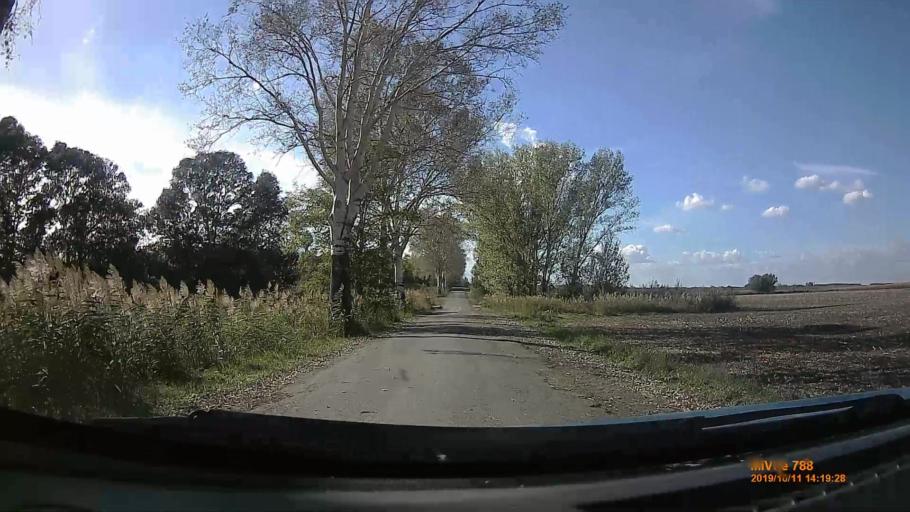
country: HU
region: Hajdu-Bihar
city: Hajduszoboszlo
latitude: 47.5294
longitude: 21.3866
